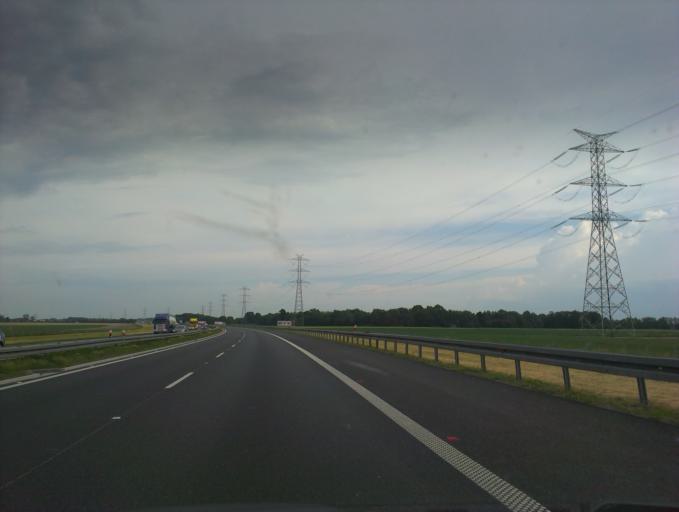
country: PL
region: Opole Voivodeship
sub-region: Powiat brzeski
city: Skarbimierz Osiedle
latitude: 50.7933
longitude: 17.3293
